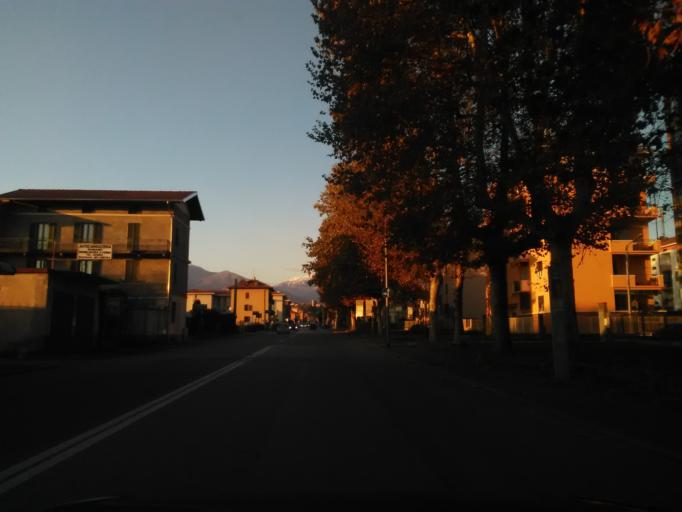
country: IT
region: Piedmont
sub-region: Provincia di Biella
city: Ponderano
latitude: 45.5460
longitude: 8.0521
